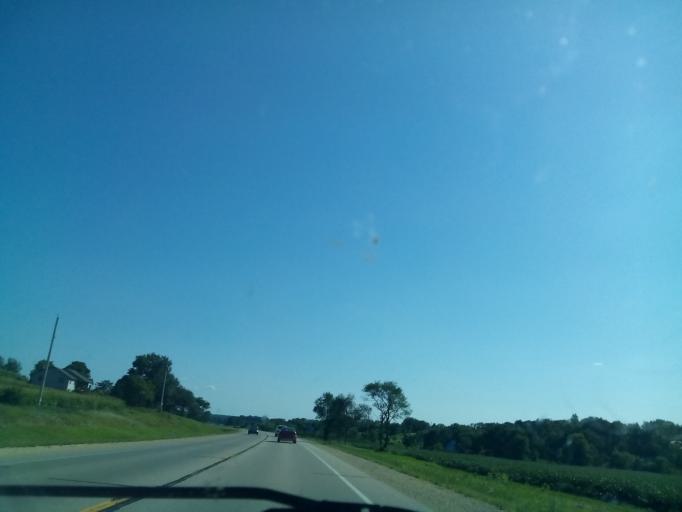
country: US
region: Wisconsin
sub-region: Green County
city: New Glarus
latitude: 42.8389
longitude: -89.6346
